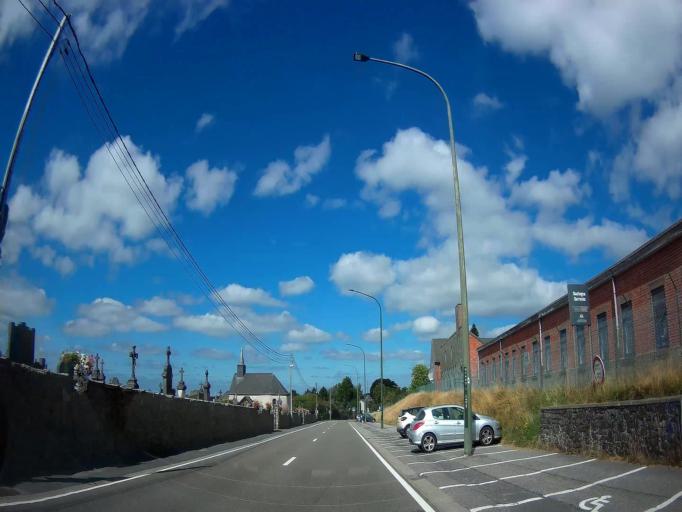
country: BE
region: Wallonia
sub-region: Province du Luxembourg
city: Bastogne
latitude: 50.0083
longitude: 5.7183
